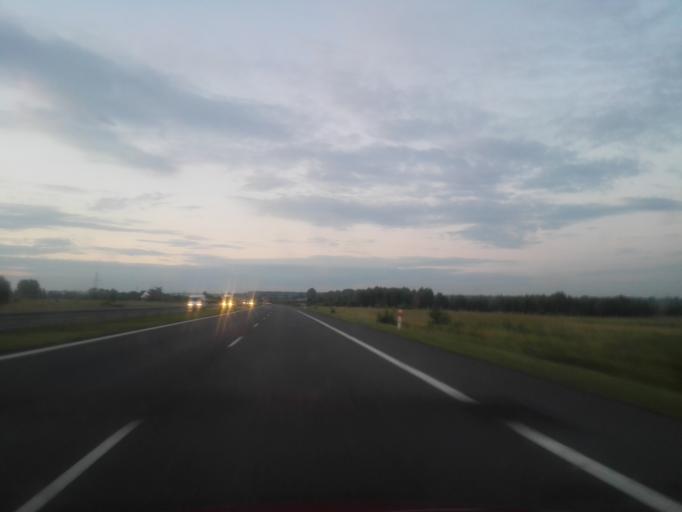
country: PL
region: Lodz Voivodeship
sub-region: Powiat piotrkowski
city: Wola Krzysztoporska
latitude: 51.3088
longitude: 19.5651
